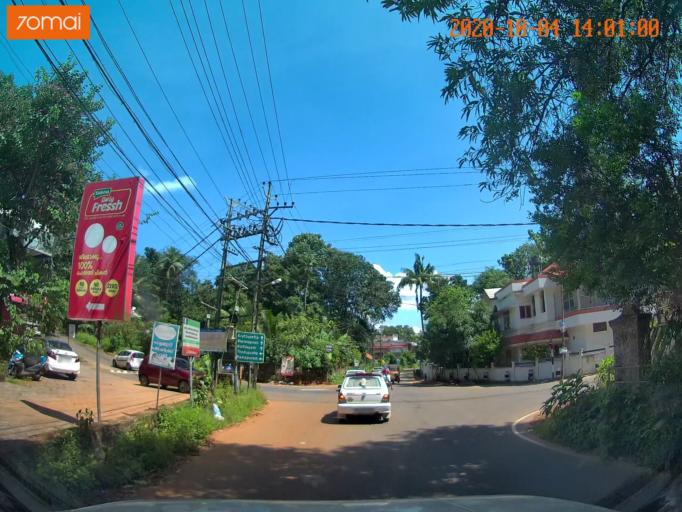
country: IN
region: Kerala
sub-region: Kottayam
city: Lalam
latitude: 9.7118
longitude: 76.6708
